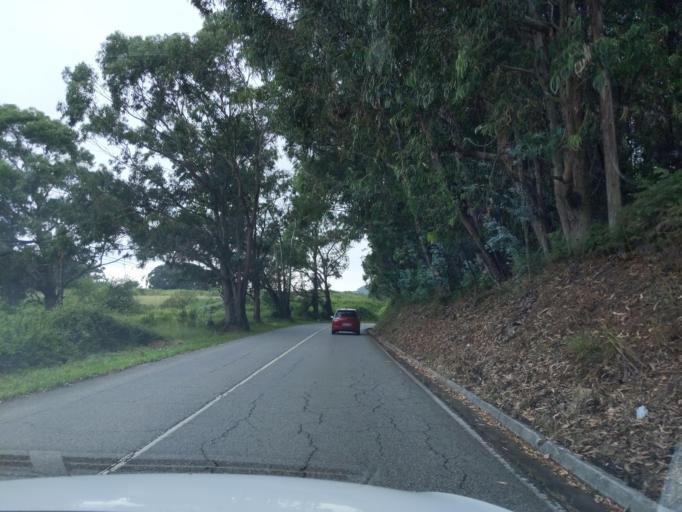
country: ES
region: Asturias
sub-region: Province of Asturias
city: Aviles
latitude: 43.5870
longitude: -5.9125
